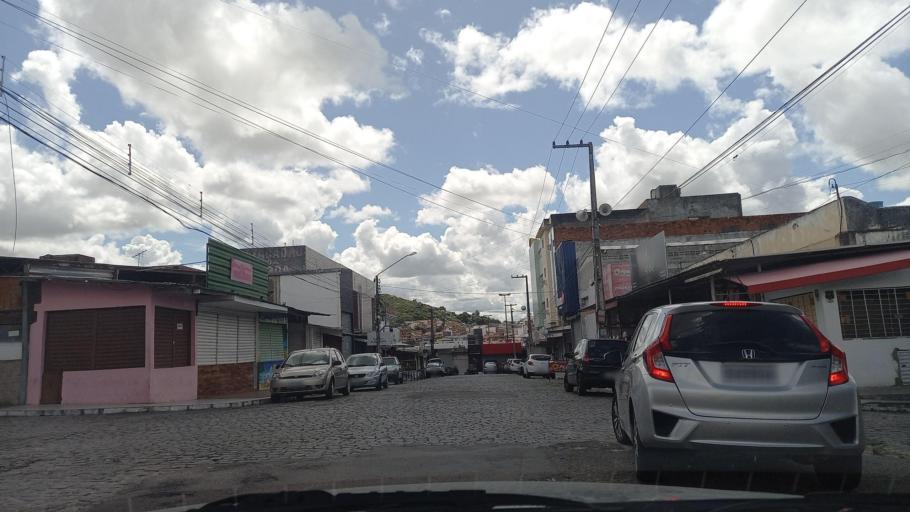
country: BR
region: Pernambuco
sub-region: Caruaru
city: Caruaru
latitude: -8.2940
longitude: -35.9731
